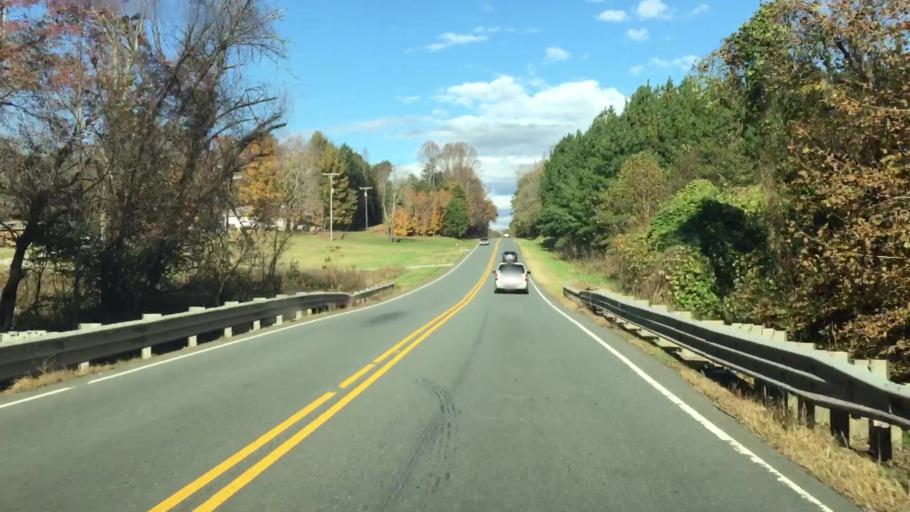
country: US
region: North Carolina
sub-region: Forsyth County
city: Walkertown
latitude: 36.2058
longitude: -80.0733
